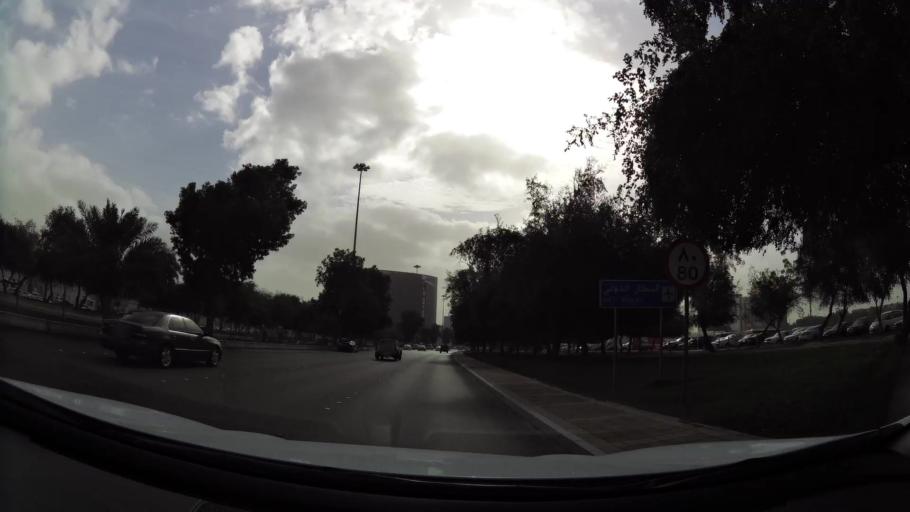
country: AE
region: Abu Dhabi
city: Abu Dhabi
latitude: 24.4240
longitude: 54.4538
